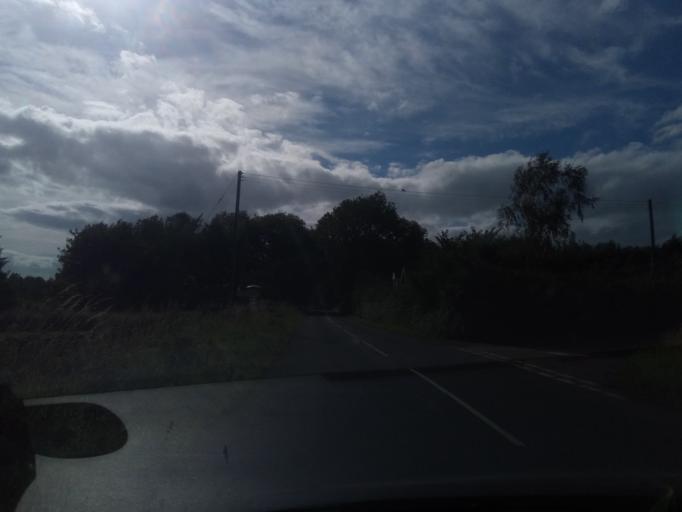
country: GB
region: Scotland
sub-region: The Scottish Borders
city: Coldstream
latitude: 55.5968
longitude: -2.2280
